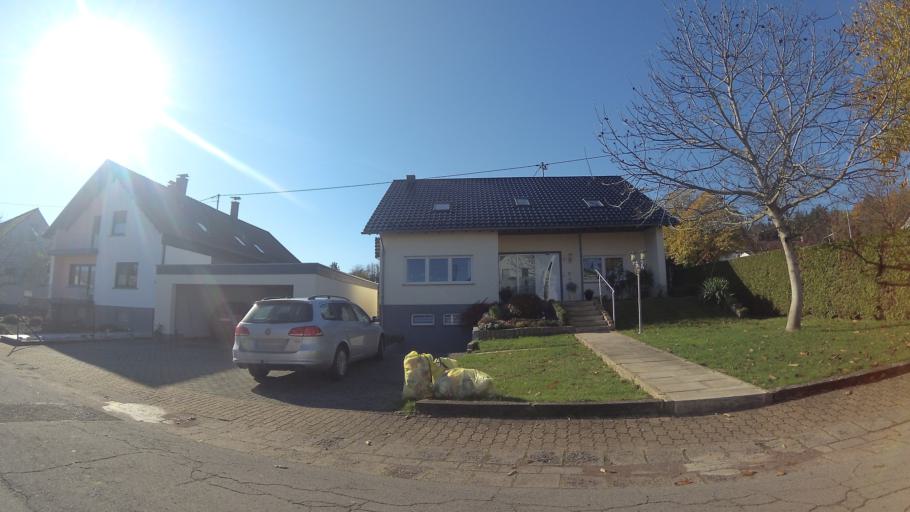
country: DE
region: Saarland
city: Losheim
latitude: 49.5326
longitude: 6.7748
